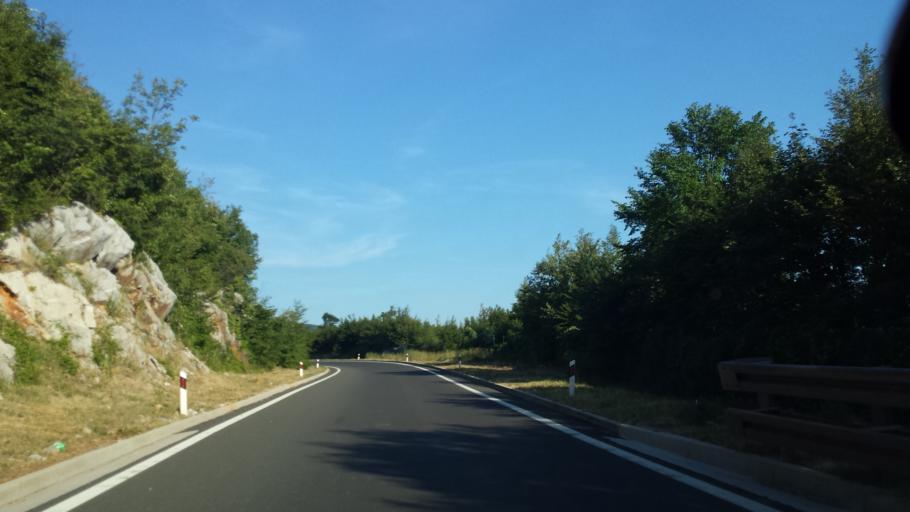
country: HR
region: Primorsko-Goranska
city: Hreljin
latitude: 45.3290
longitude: 14.6057
